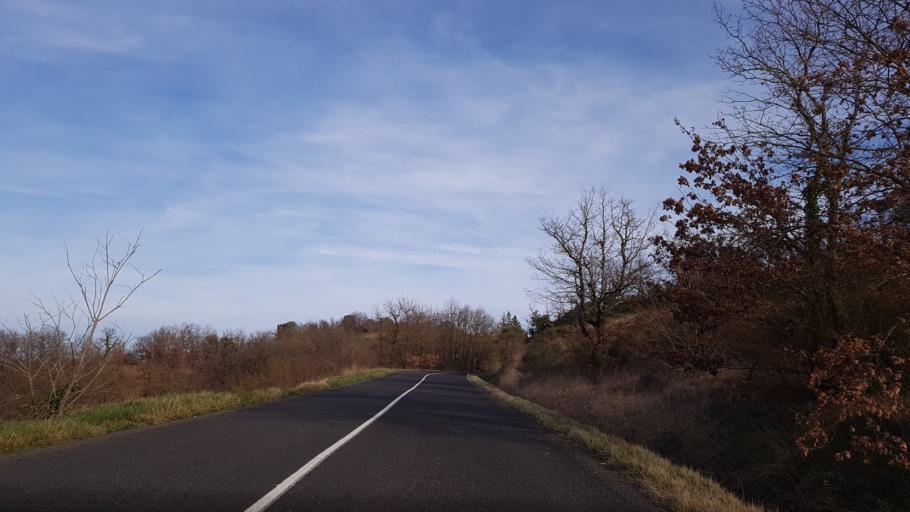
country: FR
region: Midi-Pyrenees
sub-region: Departement de l'Ariege
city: Mirepoix
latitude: 43.1340
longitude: 1.9132
